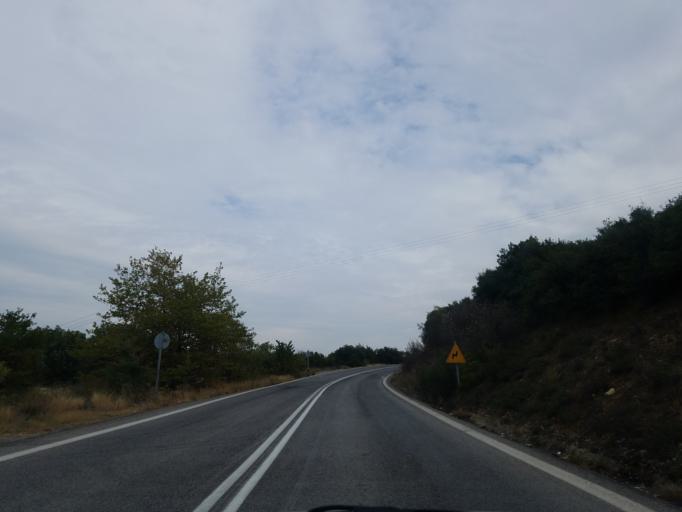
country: GR
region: Central Greece
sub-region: Nomos Fthiotidos
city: Domokos
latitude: 39.1449
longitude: 22.3048
